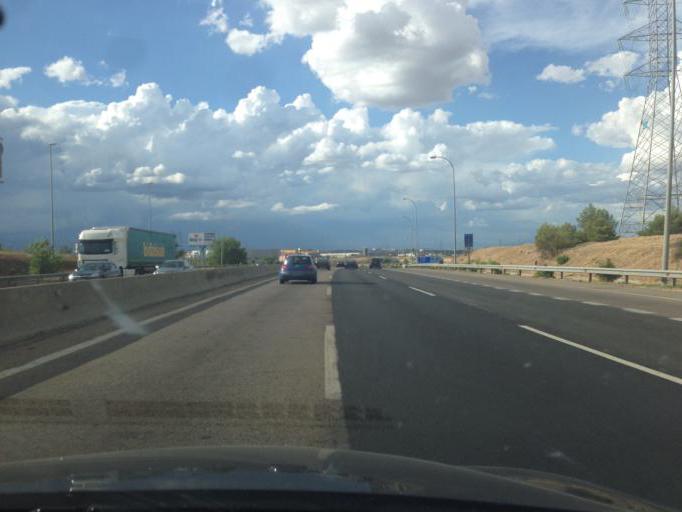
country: ES
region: Madrid
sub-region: Provincia de Madrid
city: San Sebastian de los Reyes
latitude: 40.5486
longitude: -3.6081
